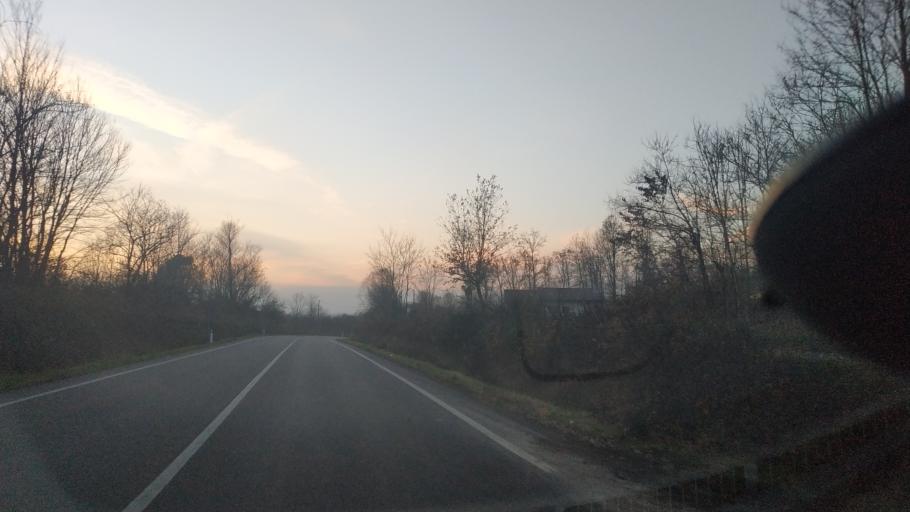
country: IT
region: Piedmont
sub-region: Provincia di Torino
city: Montanaro
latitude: 45.2435
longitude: 7.8481
